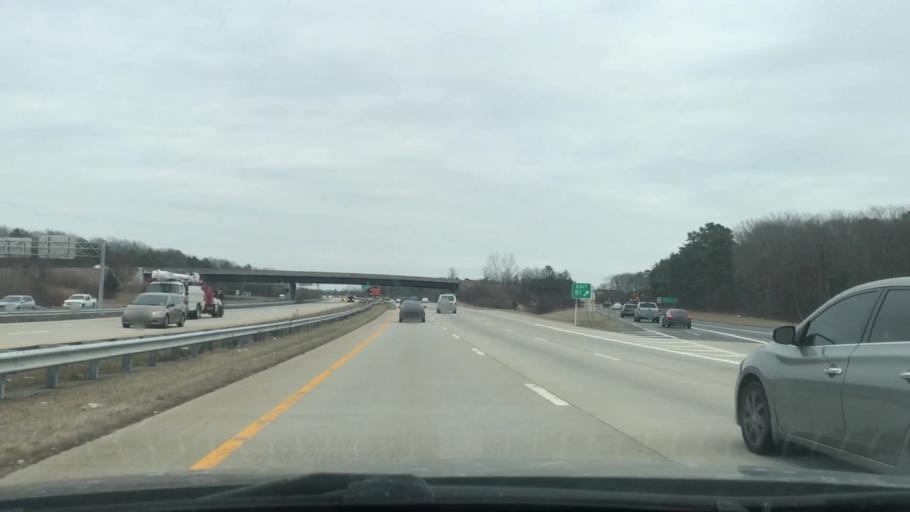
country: US
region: New York
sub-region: Suffolk County
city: Bayport
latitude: 40.7691
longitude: -73.0609
